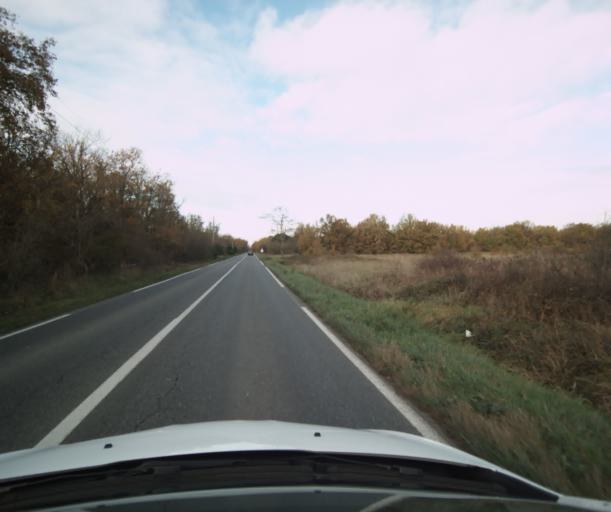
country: FR
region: Midi-Pyrenees
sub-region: Departement de la Haute-Garonne
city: Bruguieres
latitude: 43.7372
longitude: 1.4111
